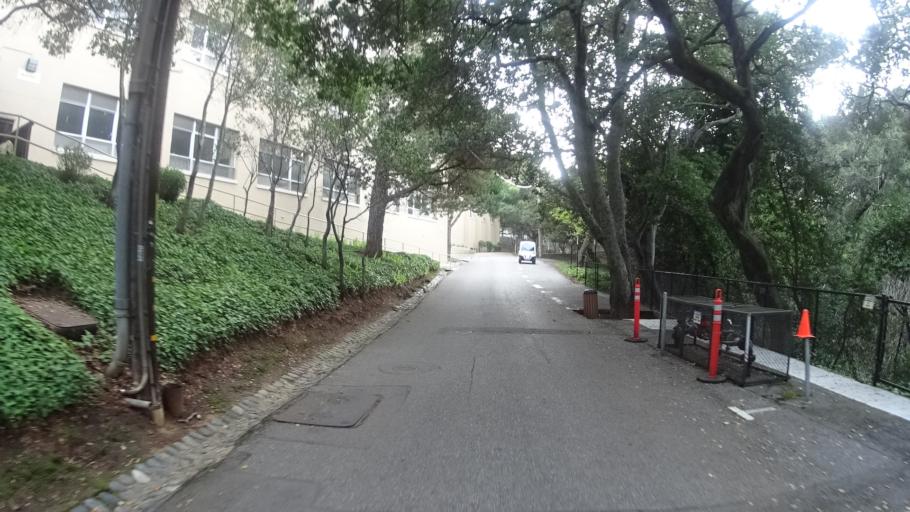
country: US
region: California
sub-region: San Mateo County
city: Hillsborough
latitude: 37.5844
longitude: -122.3835
